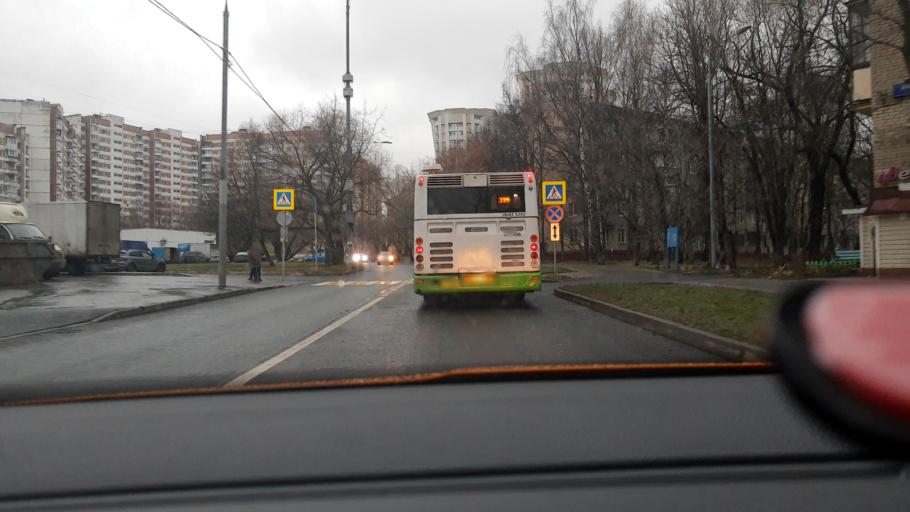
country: RU
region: Moscow
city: Strogino
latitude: 55.8457
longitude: 37.4200
